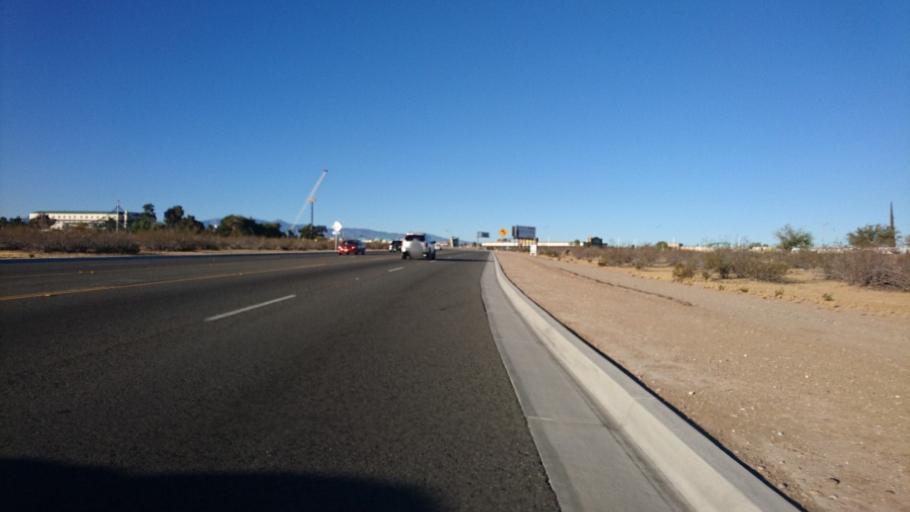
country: US
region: California
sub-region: San Bernardino County
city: Mountain View Acres
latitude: 34.4818
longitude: -117.3346
